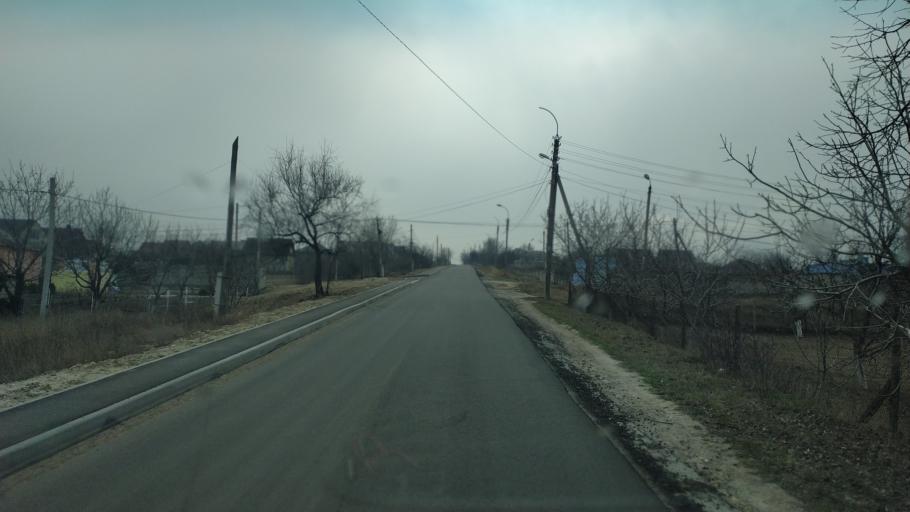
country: MD
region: Chisinau
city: Singera
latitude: 46.9112
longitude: 28.9871
